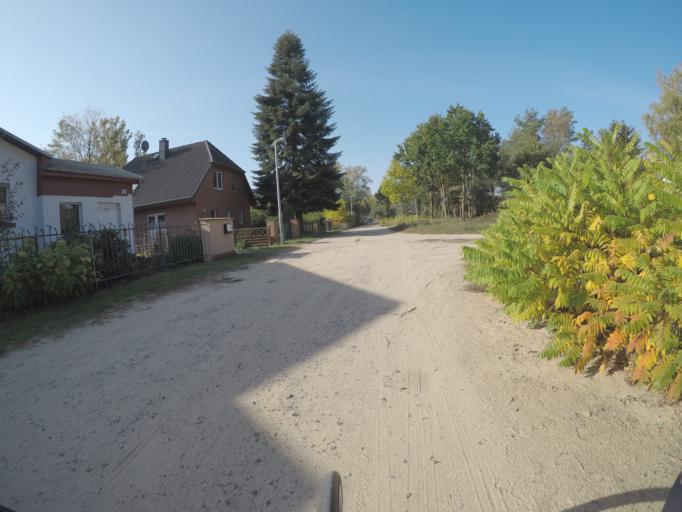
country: DE
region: Brandenburg
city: Oranienburg
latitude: 52.7305
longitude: 13.2499
